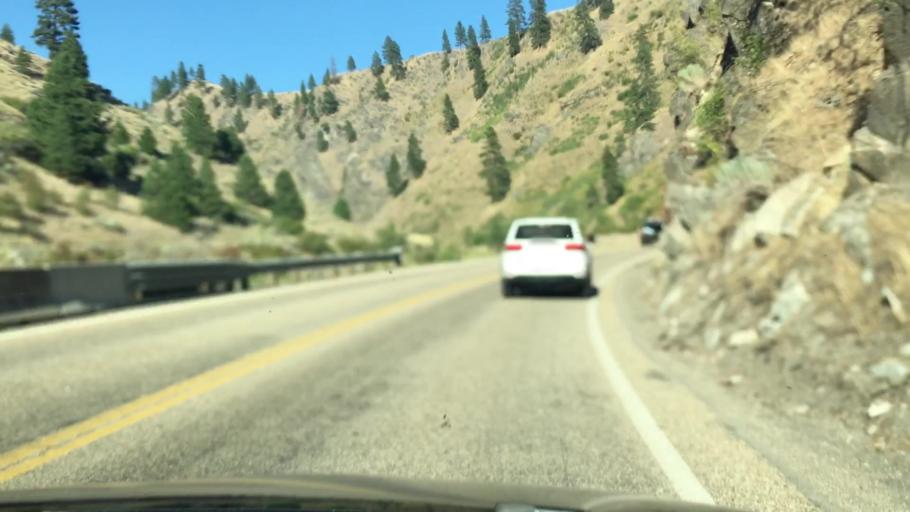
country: US
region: Idaho
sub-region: Boise County
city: Idaho City
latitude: 44.0892
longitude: -116.1101
